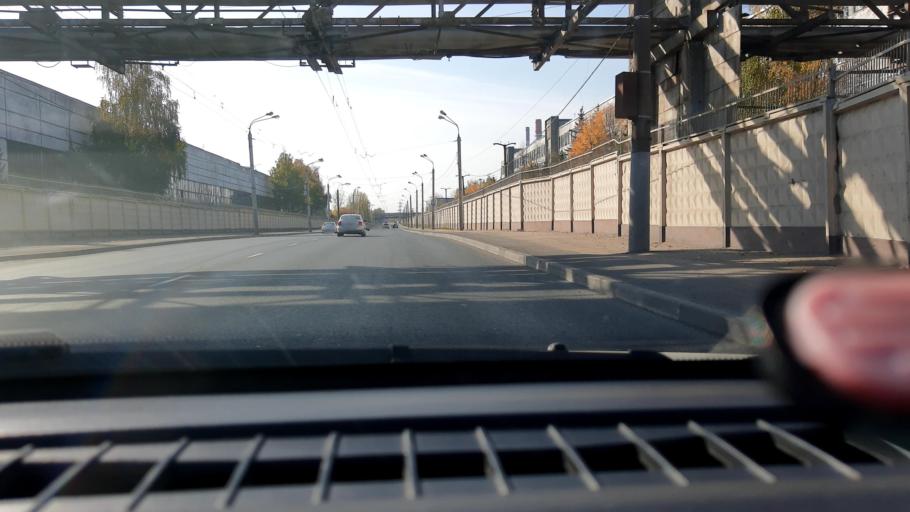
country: RU
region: Nizjnij Novgorod
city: Nizhniy Novgorod
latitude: 56.2466
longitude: 43.9126
